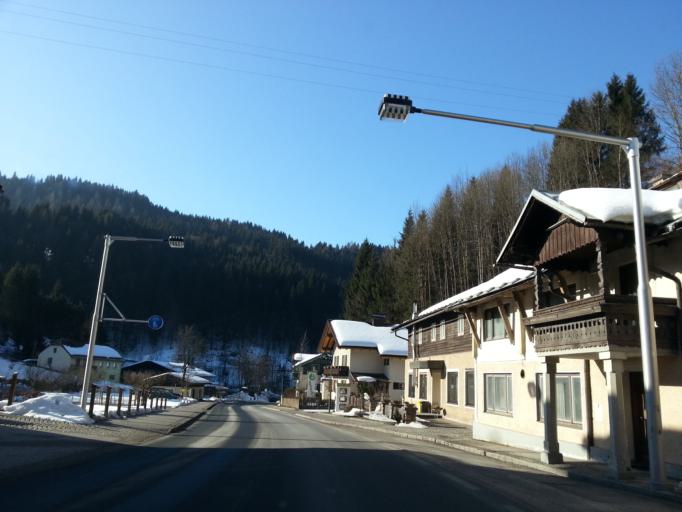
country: AT
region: Salzburg
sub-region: Politischer Bezirk Sankt Johann im Pongau
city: Huttau
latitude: 47.4235
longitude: 13.3460
